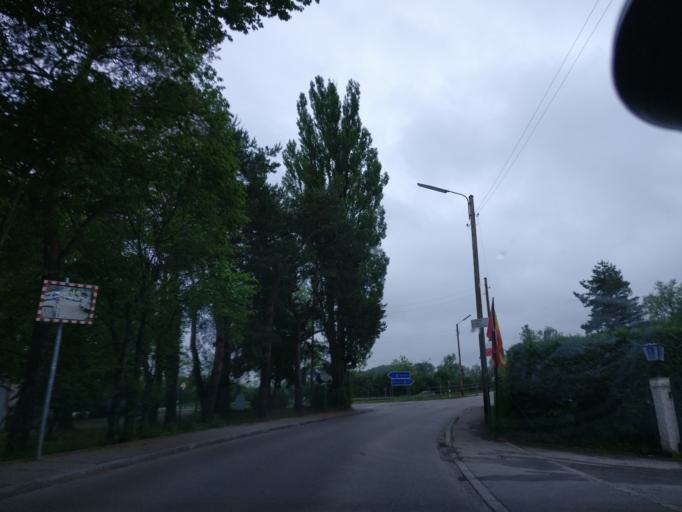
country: DE
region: Bavaria
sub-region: Upper Bavaria
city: Grobenzell
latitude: 48.1987
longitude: 11.4110
